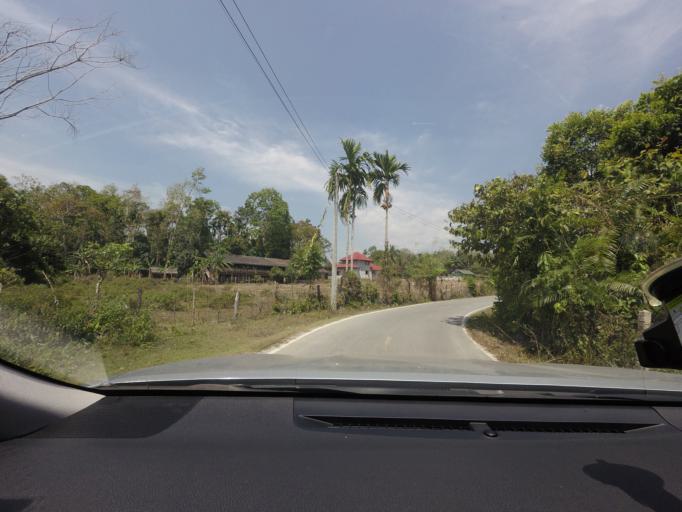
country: TH
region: Narathiwat
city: Rueso
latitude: 6.3794
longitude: 101.5023
